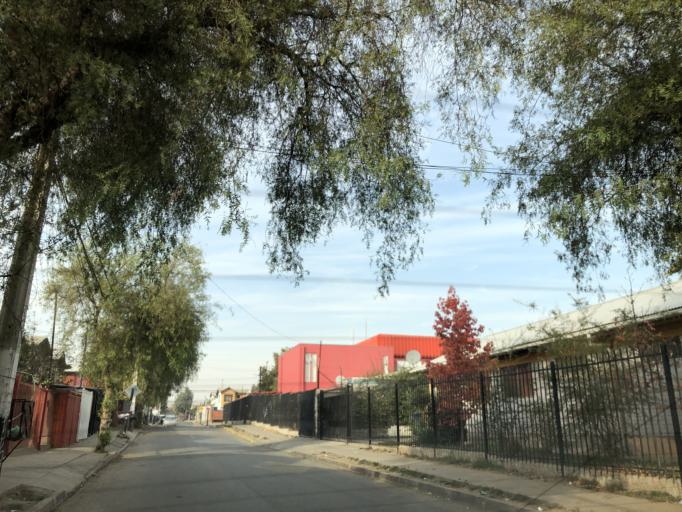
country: CL
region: Santiago Metropolitan
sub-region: Provincia de Cordillera
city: Puente Alto
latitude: -33.5835
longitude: -70.5531
